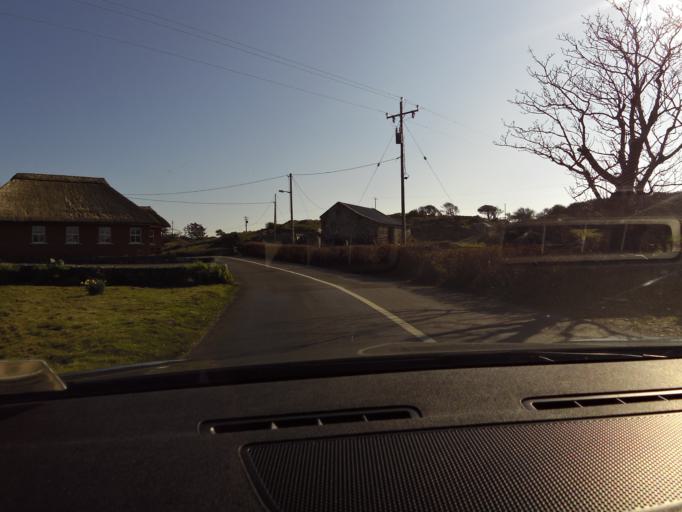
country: IE
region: Connaught
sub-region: County Galway
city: Clifden
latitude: 53.4329
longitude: -10.0760
